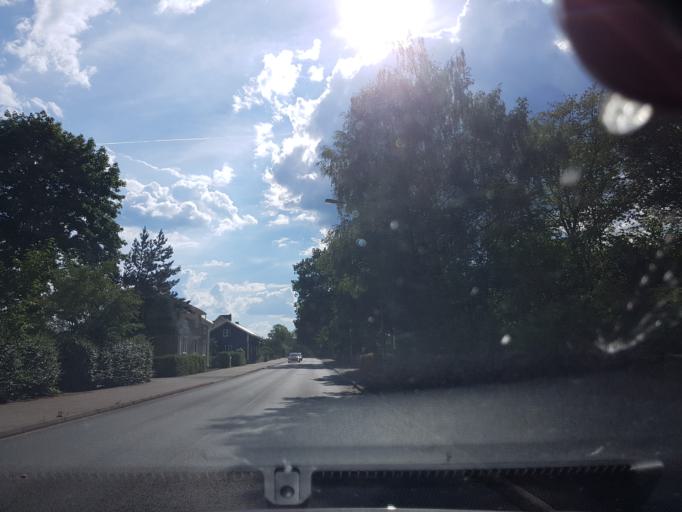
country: SE
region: Joenkoeping
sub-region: Gislaveds Kommun
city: Gislaved
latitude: 57.3004
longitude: 13.5356
